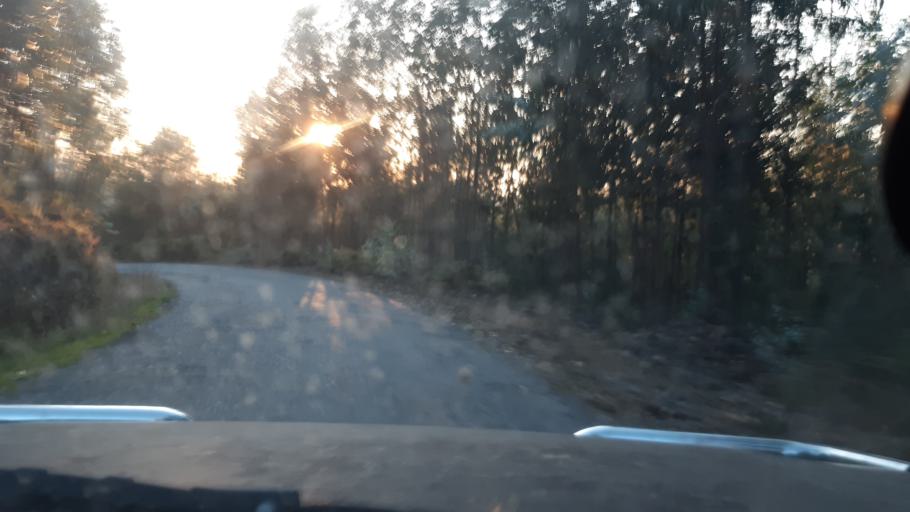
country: PT
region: Aveiro
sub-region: Agueda
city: Aguada de Cima
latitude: 40.5636
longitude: -8.3490
